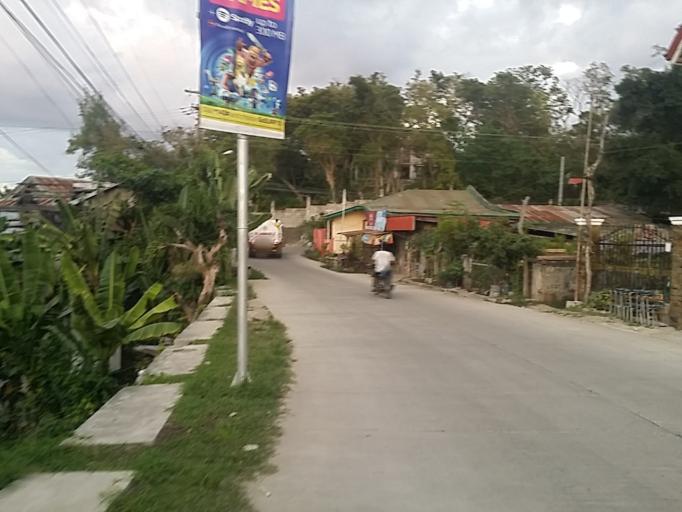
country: PH
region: Central Visayas
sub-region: Province of Cebu
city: Bogo
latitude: 11.0484
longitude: 124.0065
